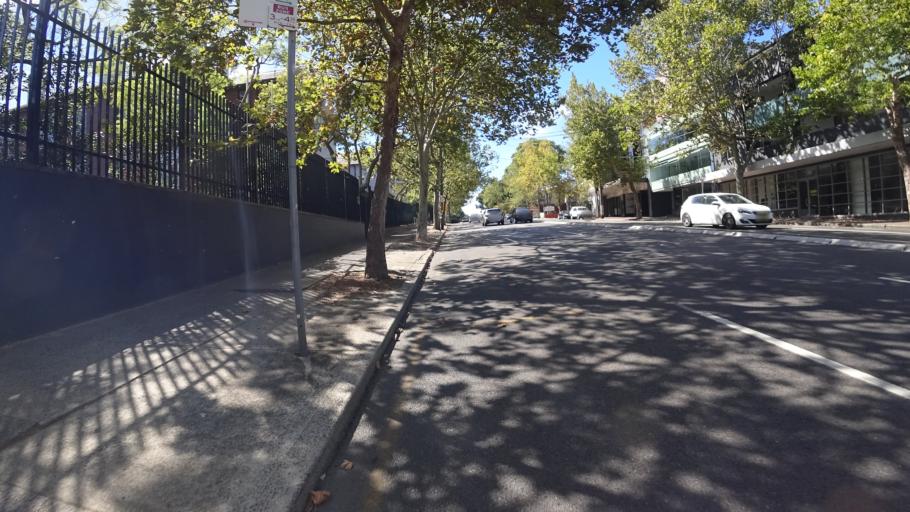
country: AU
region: New South Wales
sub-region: North Sydney
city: Crows Nest
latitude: -33.8318
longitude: 151.2038
